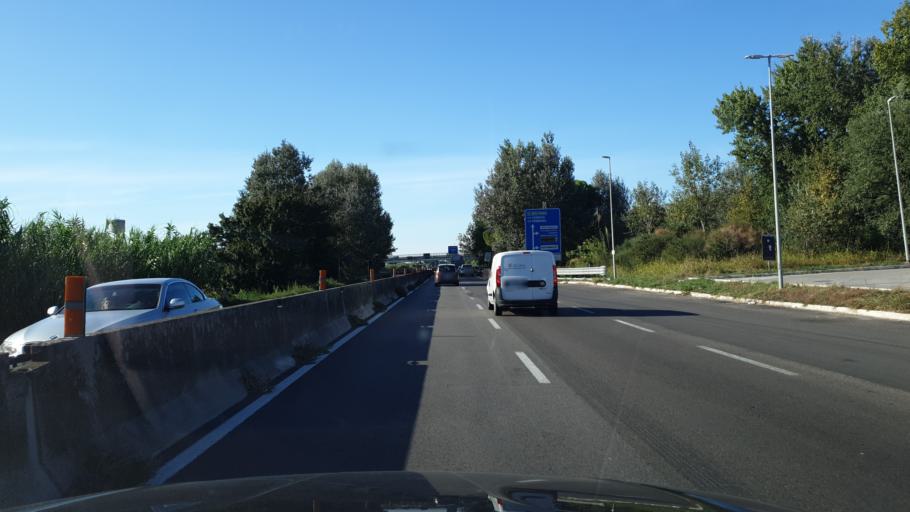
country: IT
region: Emilia-Romagna
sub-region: Provincia di Ravenna
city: Ravenna
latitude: 44.4077
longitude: 12.1748
